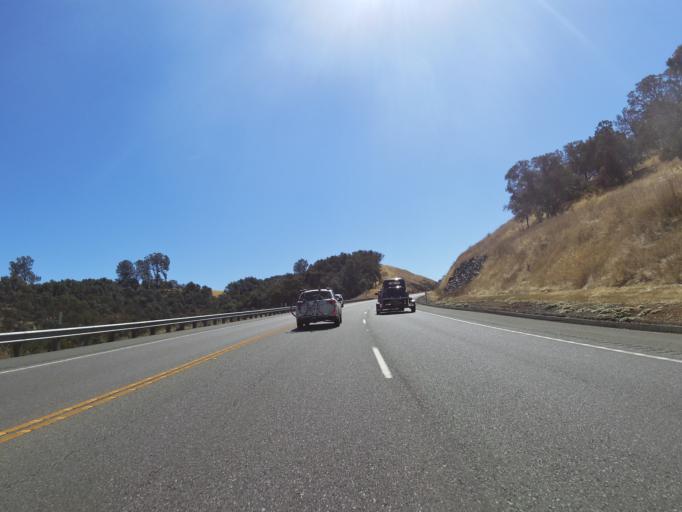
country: US
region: California
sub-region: Amador County
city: Sutter Creek
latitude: 38.4129
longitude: -120.8361
